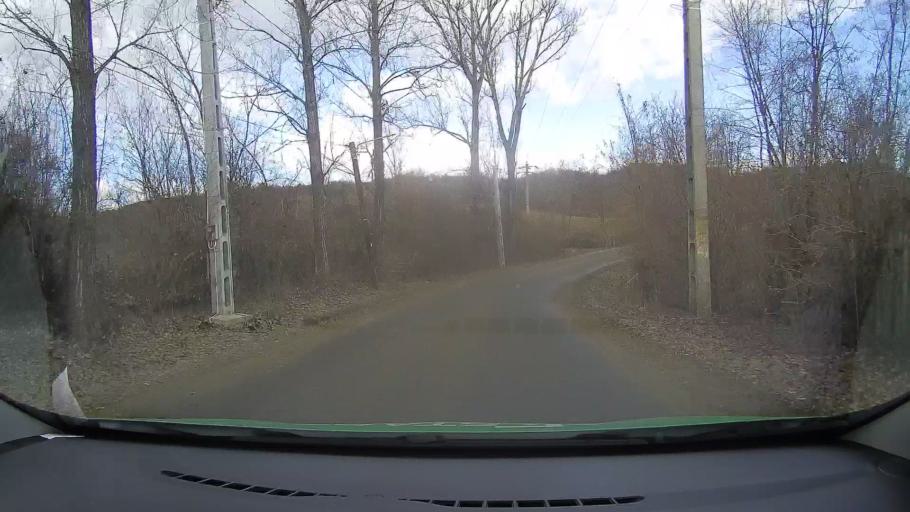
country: RO
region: Dambovita
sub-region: Comuna Buciumeni
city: Buciumeni
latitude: 45.1359
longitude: 25.4677
